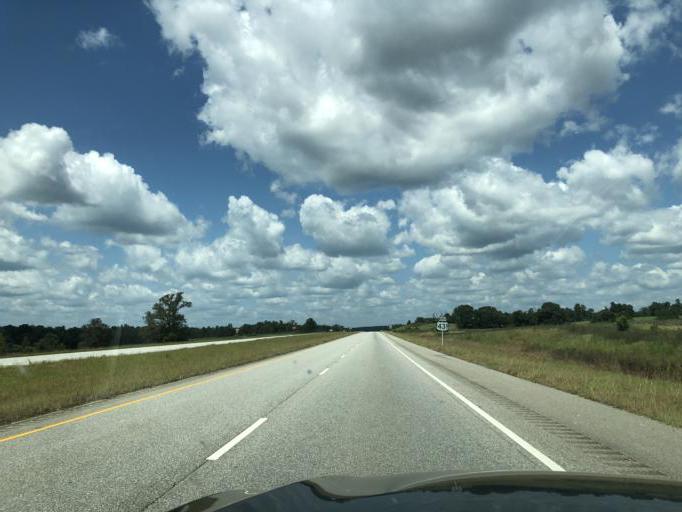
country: US
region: Alabama
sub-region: Barbour County
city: Eufaula
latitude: 32.0916
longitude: -85.1498
